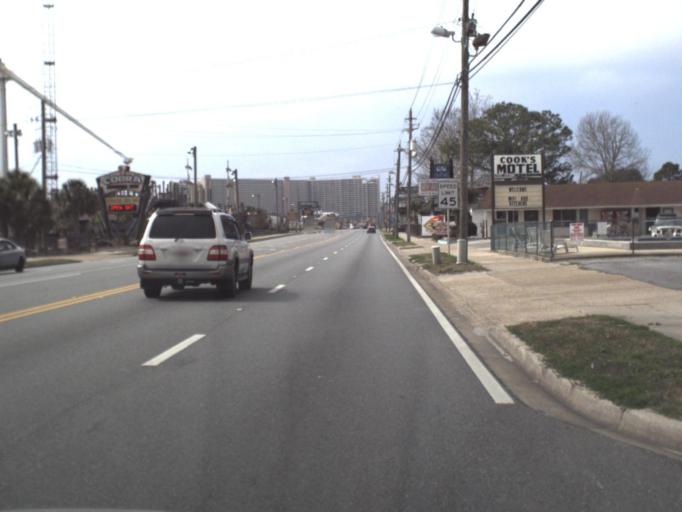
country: US
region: Florida
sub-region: Bay County
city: Panama City Beach
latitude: 30.1811
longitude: -85.7907
